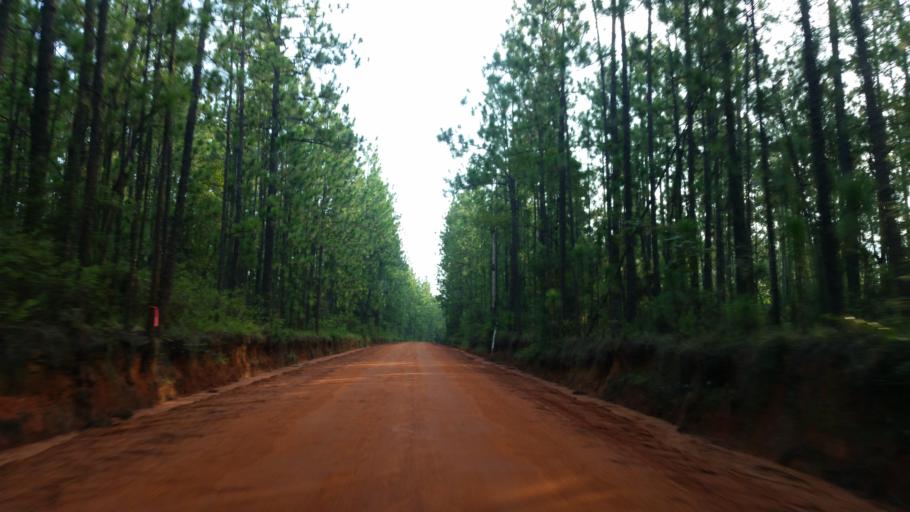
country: US
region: Alabama
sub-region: Escambia County
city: Atmore
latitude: 30.9267
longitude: -87.5732
